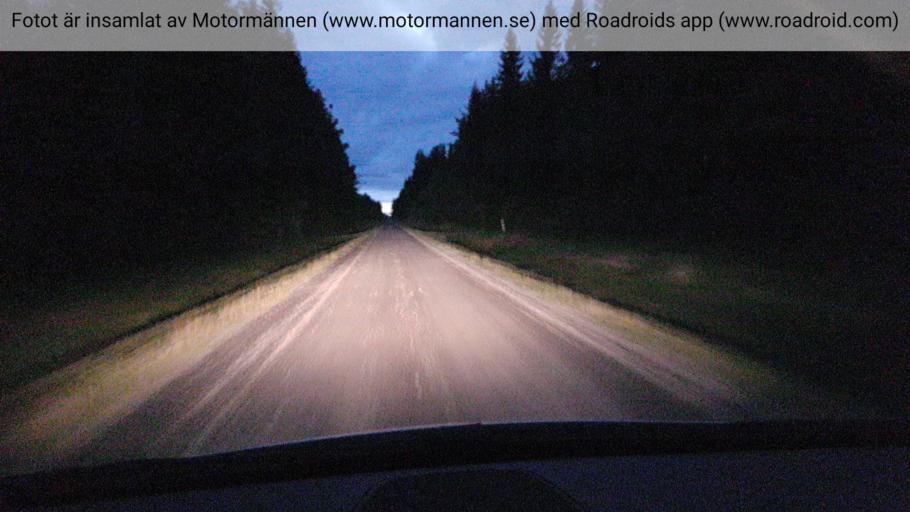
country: SE
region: Jaemtland
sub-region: Braecke Kommun
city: Braecke
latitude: 63.2849
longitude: 15.3681
